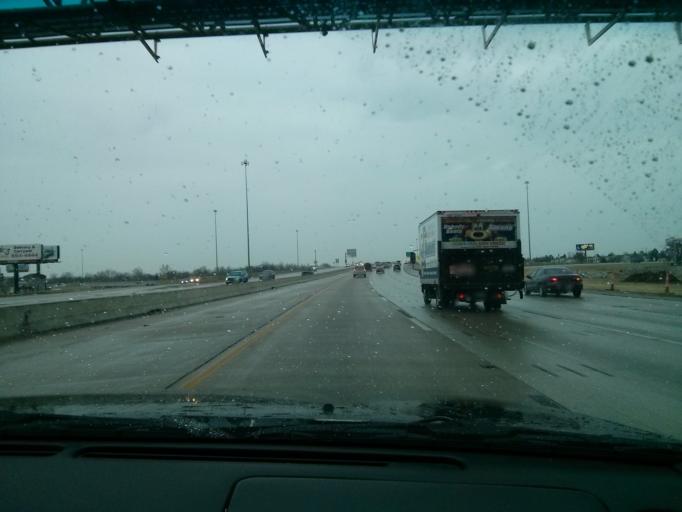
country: US
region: Oklahoma
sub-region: Tulsa County
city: Broken Arrow
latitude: 36.0944
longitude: -95.8596
